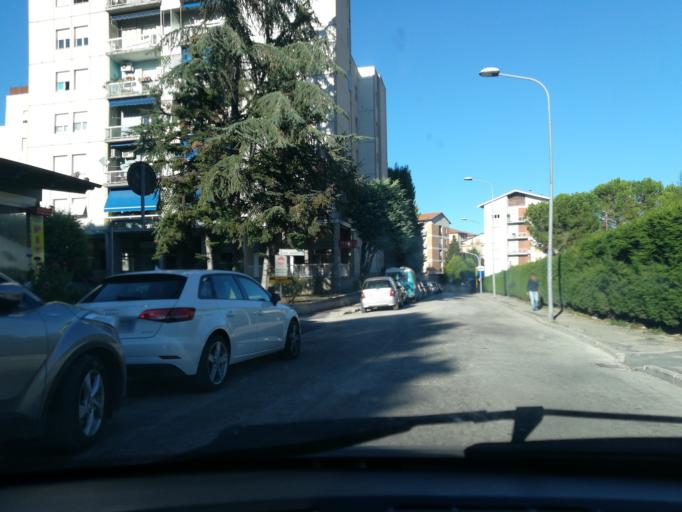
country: IT
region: The Marches
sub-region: Provincia di Macerata
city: Tolentino
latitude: 43.2107
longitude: 13.2884
